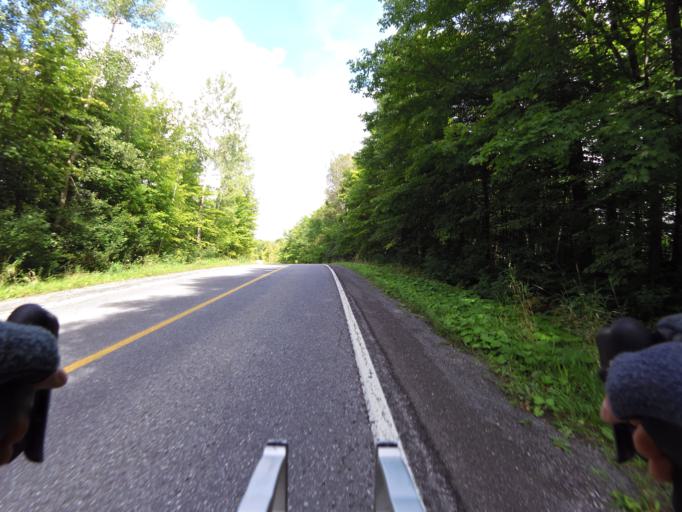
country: CA
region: Quebec
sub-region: Outaouais
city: Gatineau
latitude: 45.5002
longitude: -75.7471
